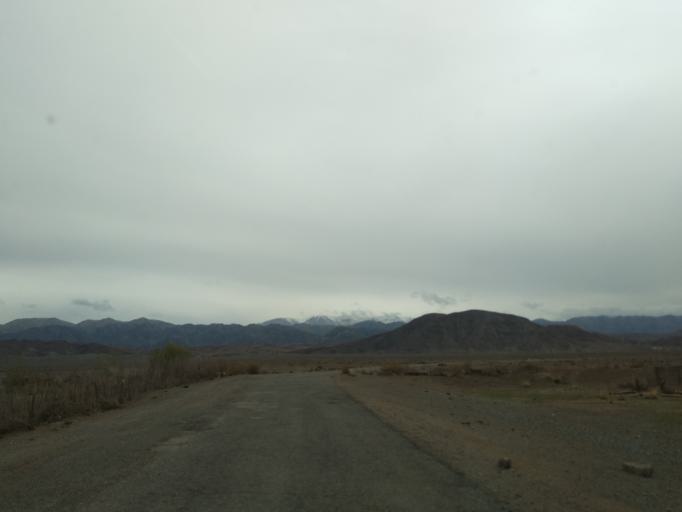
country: KG
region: Ysyk-Koel
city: Balykchy
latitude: 42.3204
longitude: 76.2342
